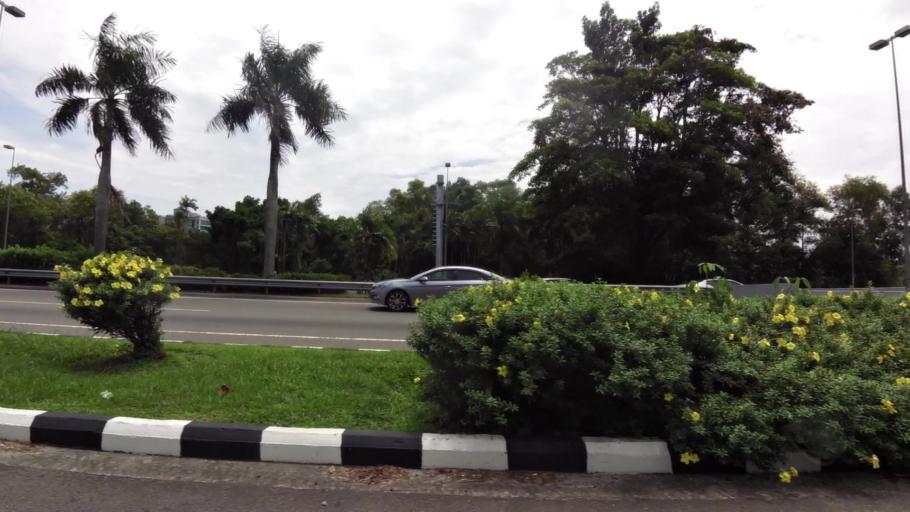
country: BN
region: Brunei and Muara
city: Bandar Seri Begawan
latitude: 4.9065
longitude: 114.9205
